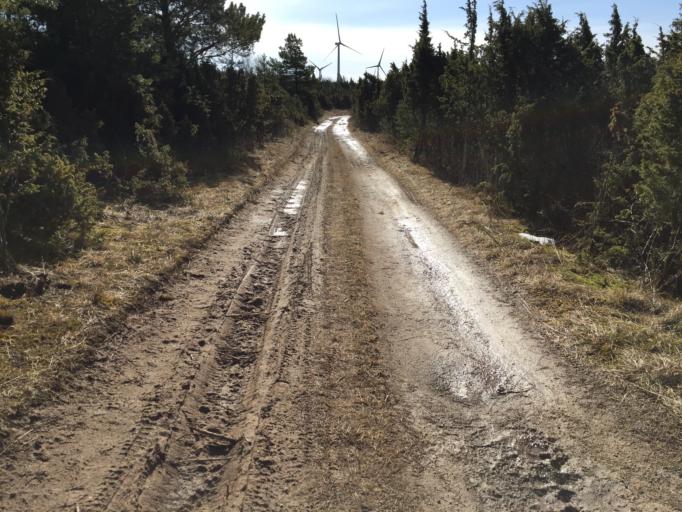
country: EE
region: Laeaene
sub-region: Haapsalu linn
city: Haapsalu
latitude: 58.6479
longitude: 23.5104
